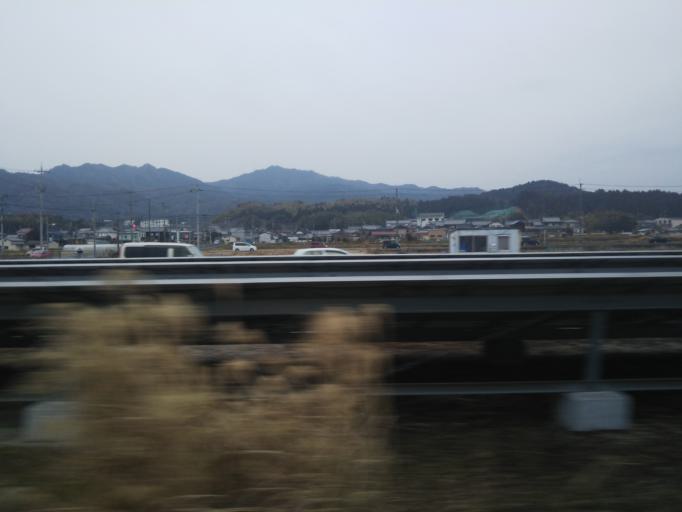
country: JP
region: Shiga Prefecture
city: Minakuchicho-matoba
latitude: 34.9978
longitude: 136.0871
